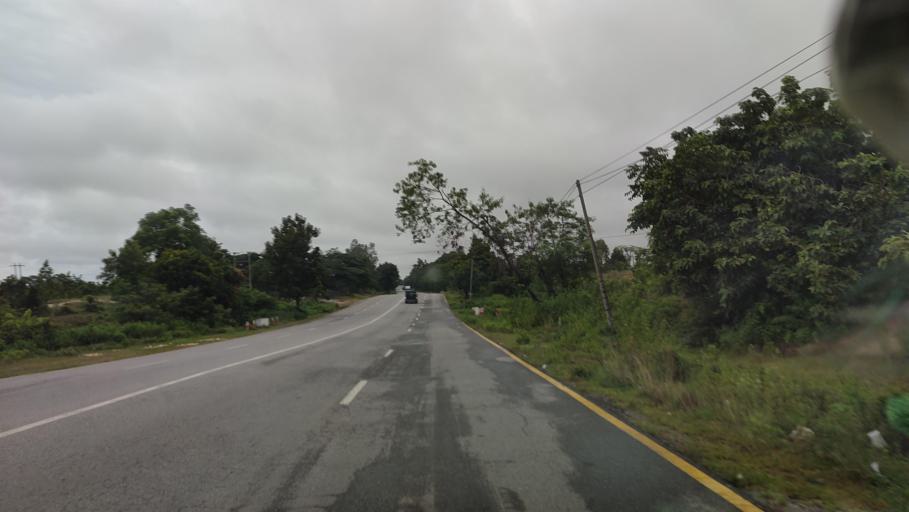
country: MM
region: Mandalay
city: Pyinmana
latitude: 20.0020
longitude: 96.2477
